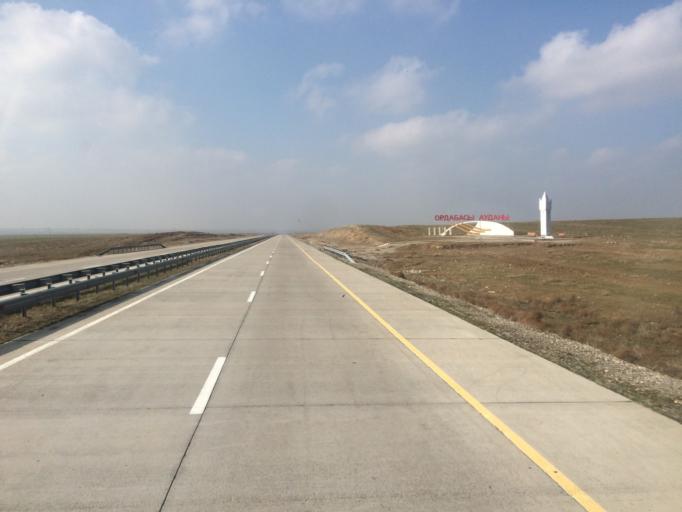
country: KZ
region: Ongtustik Qazaqstan
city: Temirlanovka
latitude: 42.5159
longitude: 69.4267
